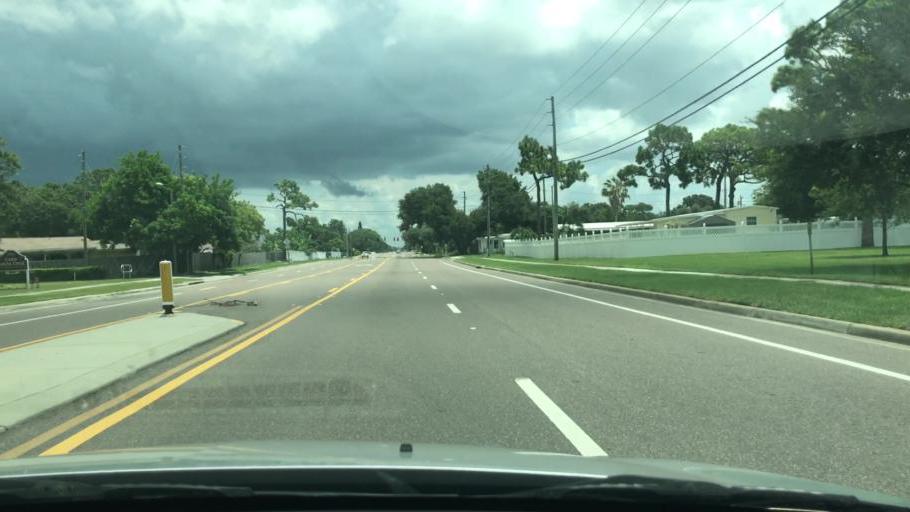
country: US
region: Florida
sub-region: Pinellas County
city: Kenneth City
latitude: 27.8209
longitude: -82.7468
